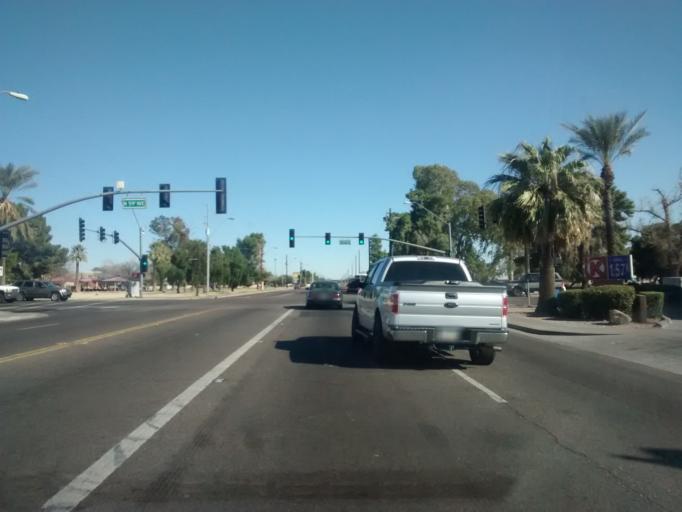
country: US
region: Arizona
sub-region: Maricopa County
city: Glendale
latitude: 33.5241
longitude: -112.1869
